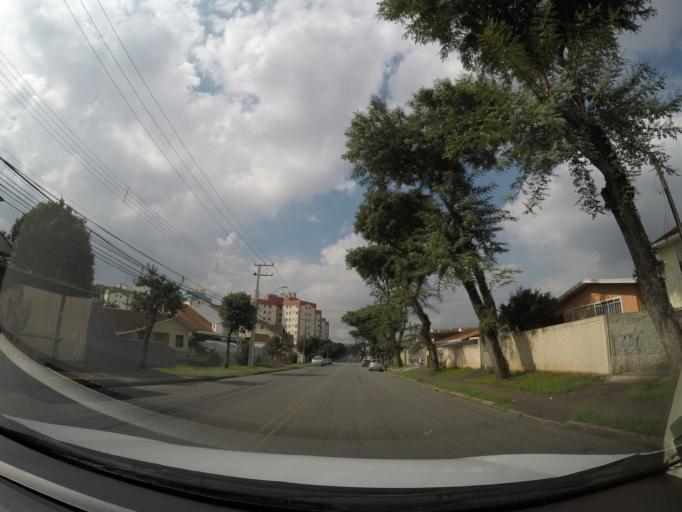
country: BR
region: Parana
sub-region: Curitiba
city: Curitiba
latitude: -25.4865
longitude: -49.2558
